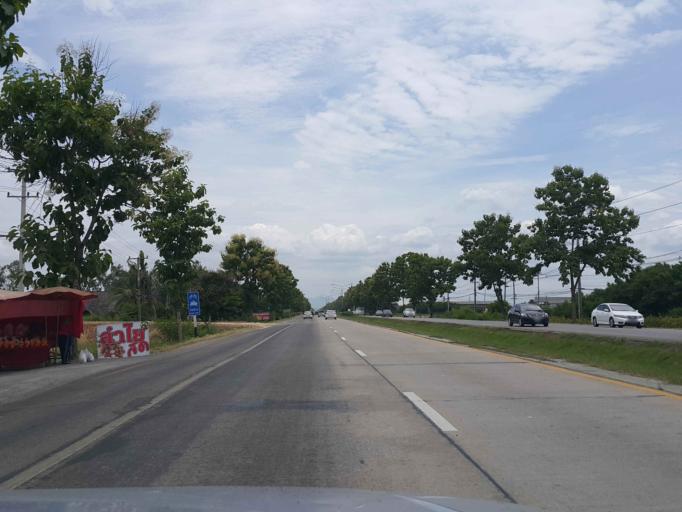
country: TH
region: Chiang Mai
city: Saraphi
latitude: 18.6752
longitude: 99.0511
